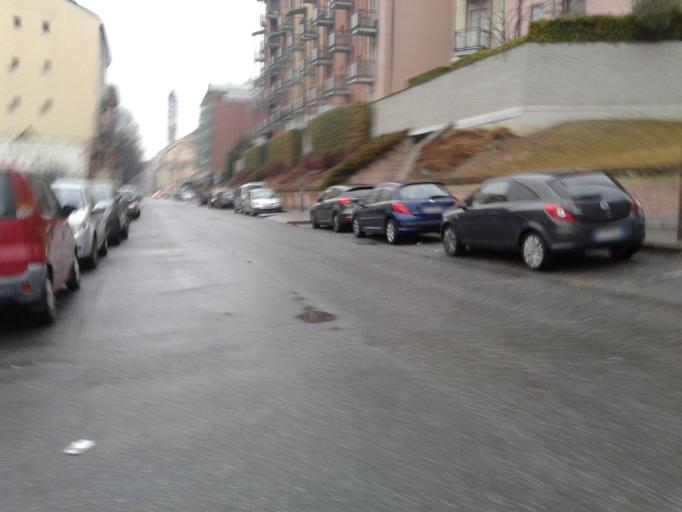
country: IT
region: Piedmont
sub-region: Provincia di Torino
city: Turin
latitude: 45.0843
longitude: 7.6711
